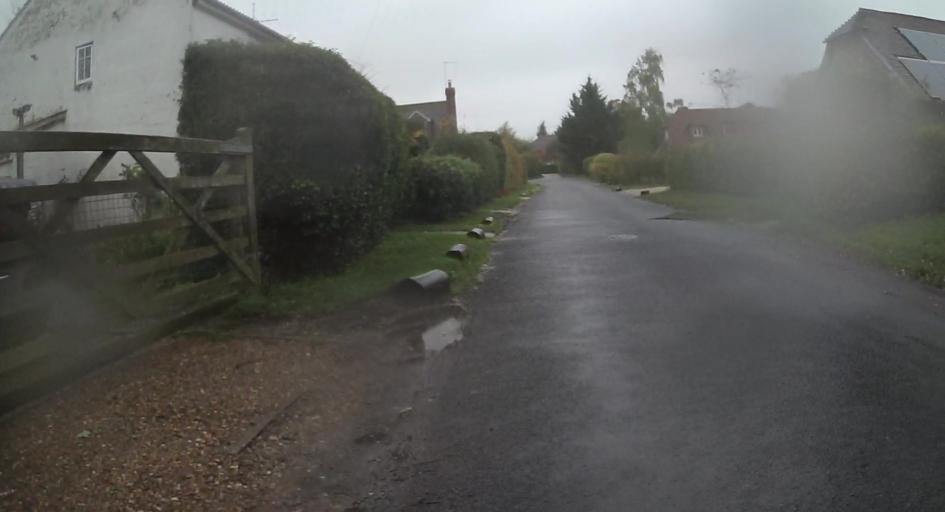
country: GB
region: England
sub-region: Hampshire
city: Kingsley
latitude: 51.1938
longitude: -0.8749
